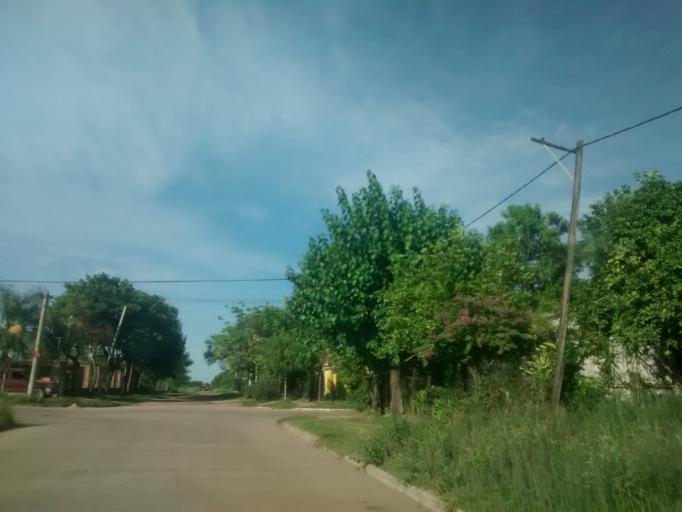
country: AR
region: Chaco
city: Puerto Tirol
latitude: -27.3762
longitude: -59.0920
